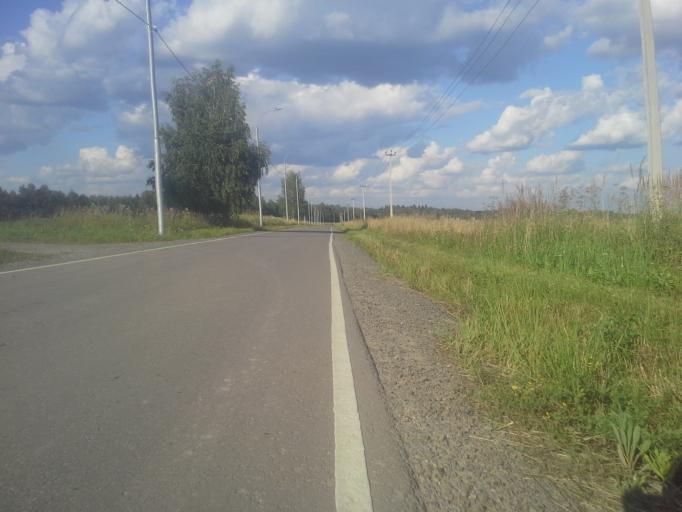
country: RU
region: Moskovskaya
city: Selyatino
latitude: 55.4283
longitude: 37.0217
